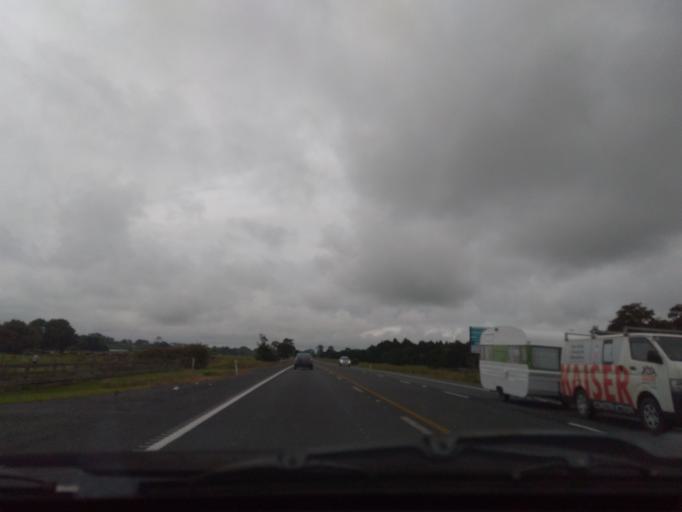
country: NZ
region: Northland
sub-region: Whangarei
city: Ruakaka
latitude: -35.8746
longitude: 174.4080
